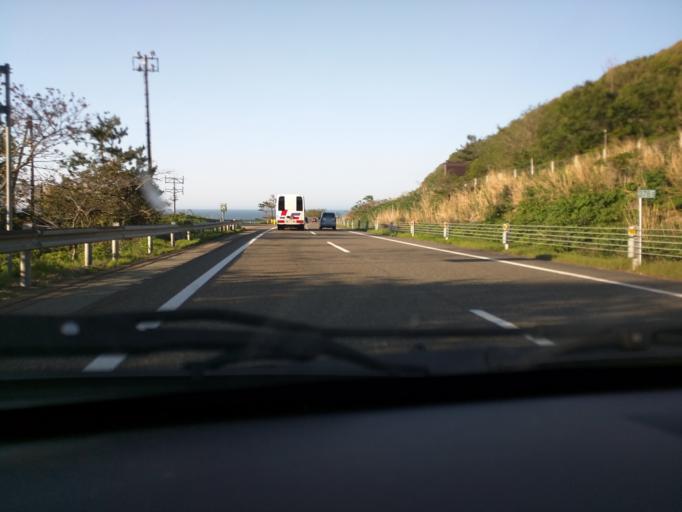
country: JP
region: Niigata
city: Kashiwazaki
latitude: 37.3036
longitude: 138.4182
